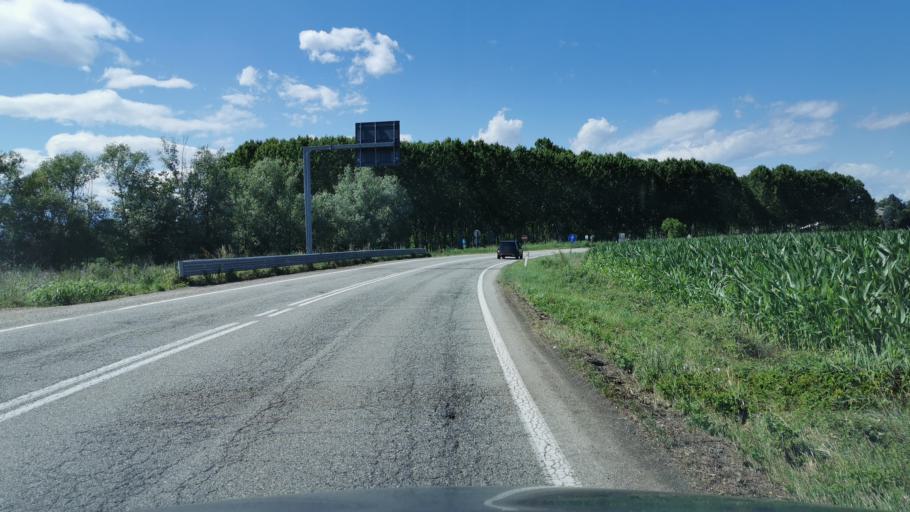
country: IT
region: Piedmont
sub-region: Provincia di Torino
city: Airasca
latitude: 44.9205
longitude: 7.4941
